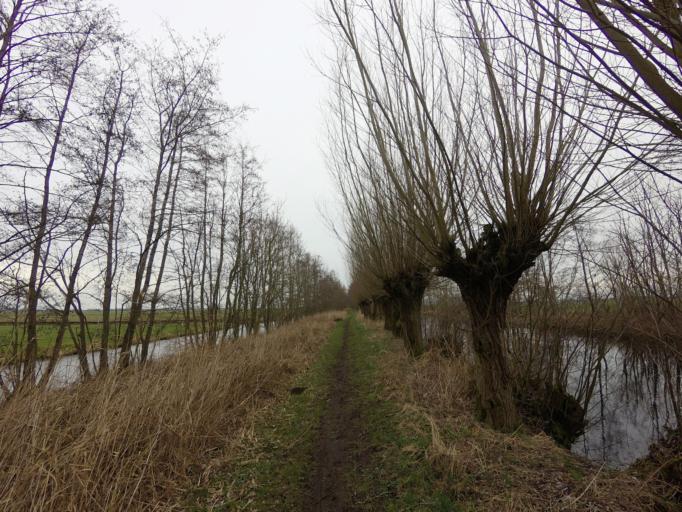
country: NL
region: South Holland
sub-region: Gemeente Vlist
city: Vlist
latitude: 51.9898
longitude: 4.8469
